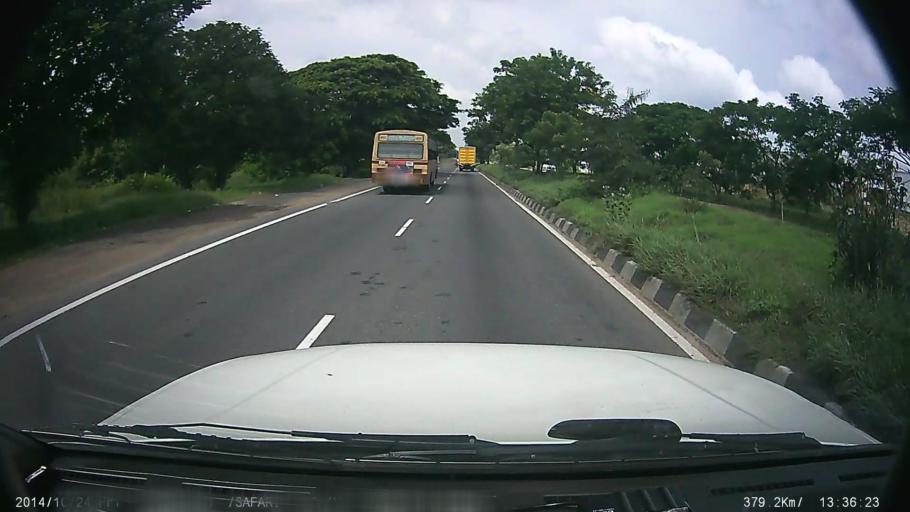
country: IN
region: Tamil Nadu
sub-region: Kancheepuram
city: Singapperumalkovil
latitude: 12.7792
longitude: 80.0113
